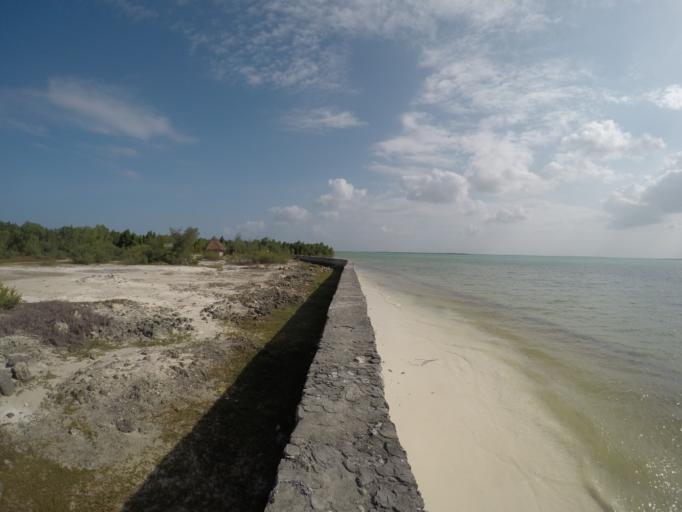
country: TZ
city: Kiwengwa
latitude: -6.1450
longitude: 39.4891
